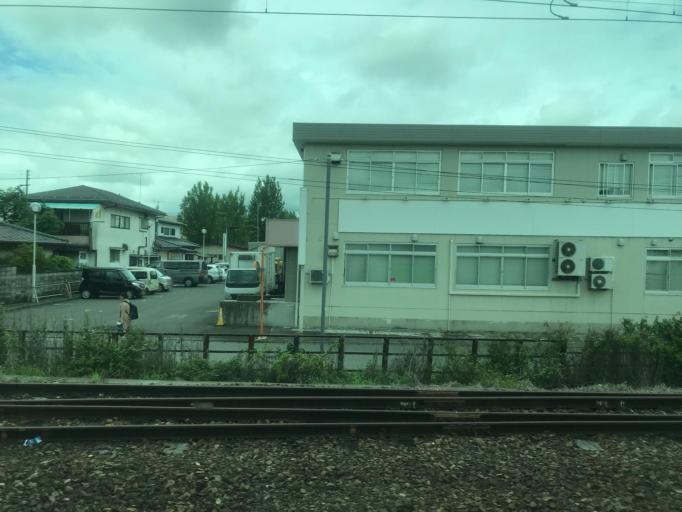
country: JP
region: Fukushima
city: Koriyama
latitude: 37.3583
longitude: 140.3694
